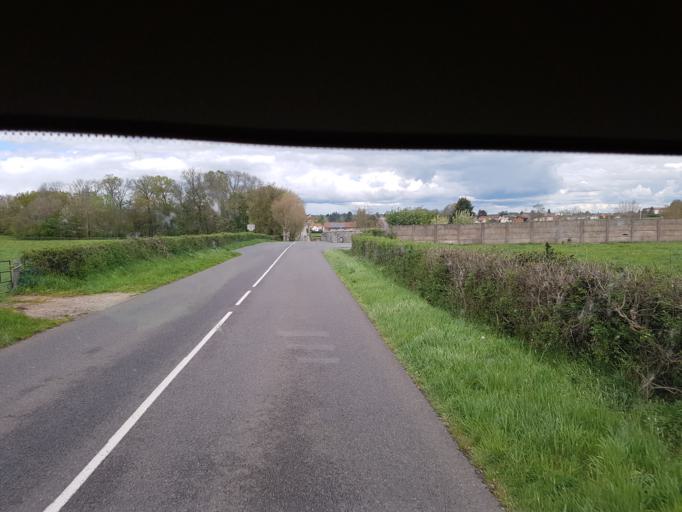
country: FR
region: Bourgogne
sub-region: Departement de Saone-et-Loire
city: Genelard
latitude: 46.5707
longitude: 4.2354
